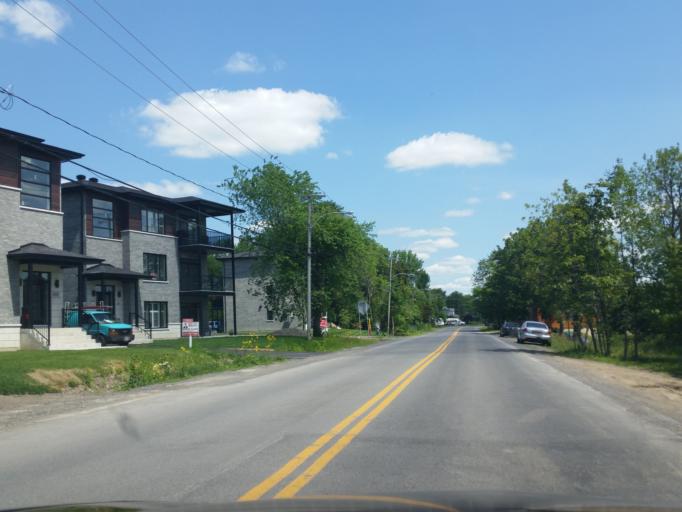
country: CA
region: Quebec
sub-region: Monteregie
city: Saint-Jean-sur-Richelieu
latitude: 45.3710
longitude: -73.2602
